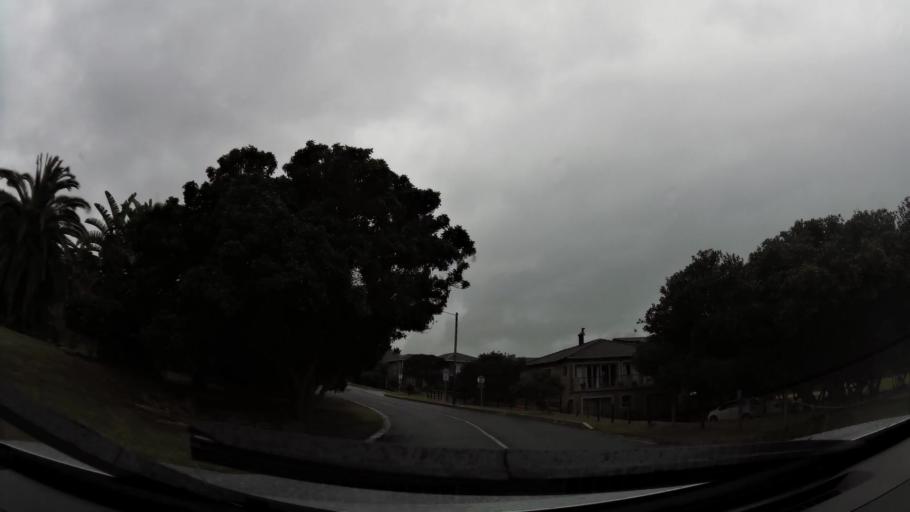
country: ZA
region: Western Cape
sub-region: Eden District Municipality
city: Mossel Bay
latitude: -34.0514
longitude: 22.2447
